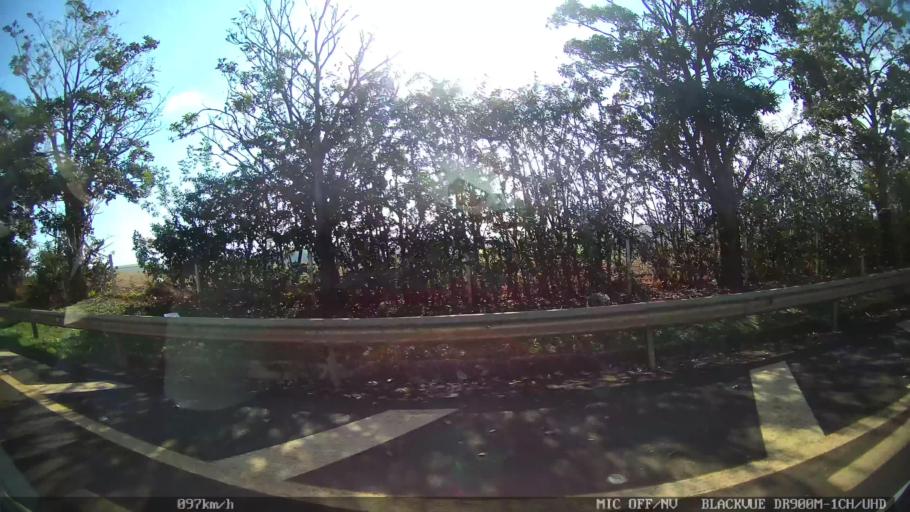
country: BR
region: Sao Paulo
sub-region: Piracicaba
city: Piracicaba
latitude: -22.6755
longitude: -47.5613
